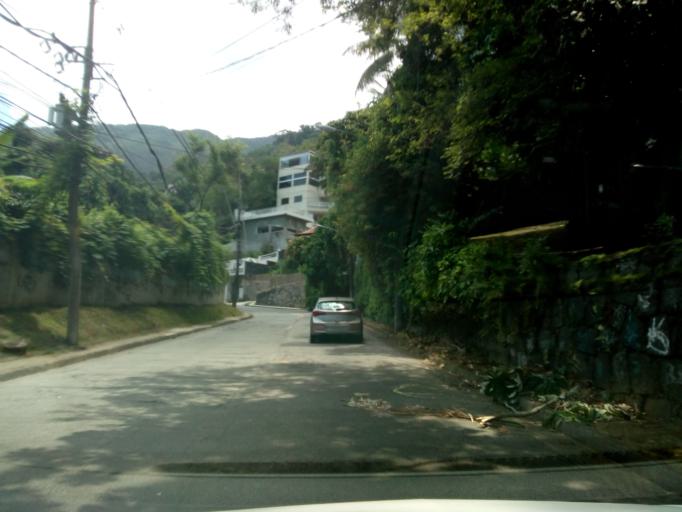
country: BR
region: Rio de Janeiro
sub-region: Rio De Janeiro
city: Rio de Janeiro
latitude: -22.9830
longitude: -43.2994
